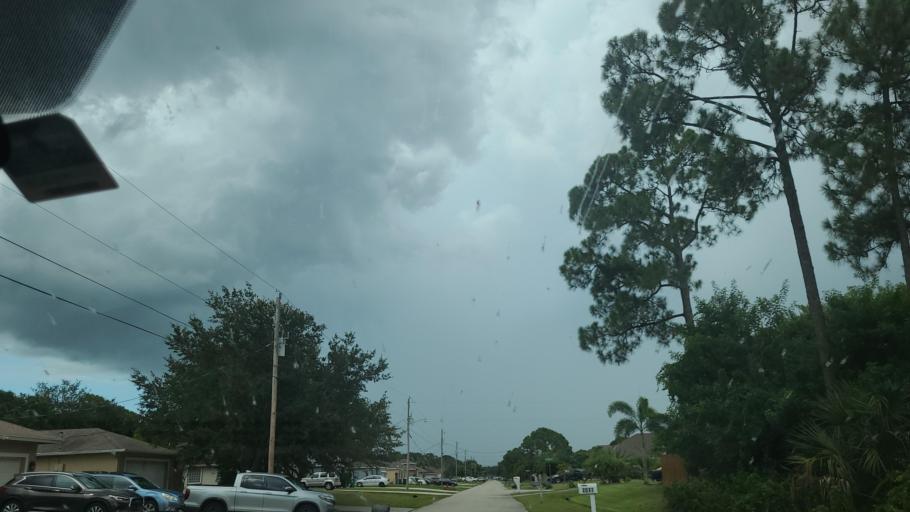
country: US
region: Florida
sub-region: Saint Lucie County
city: Port Saint Lucie
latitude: 27.2529
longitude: -80.4108
